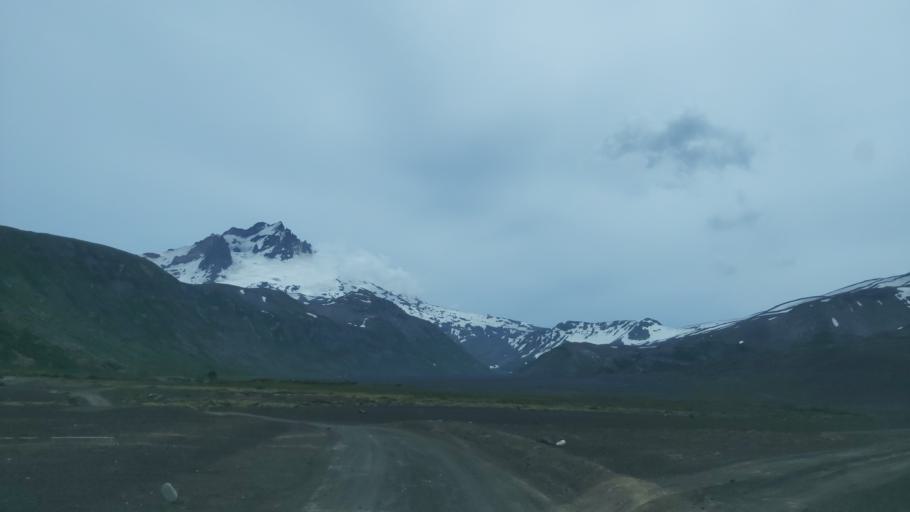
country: AR
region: Neuquen
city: Andacollo
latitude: -37.4613
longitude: -71.3127
